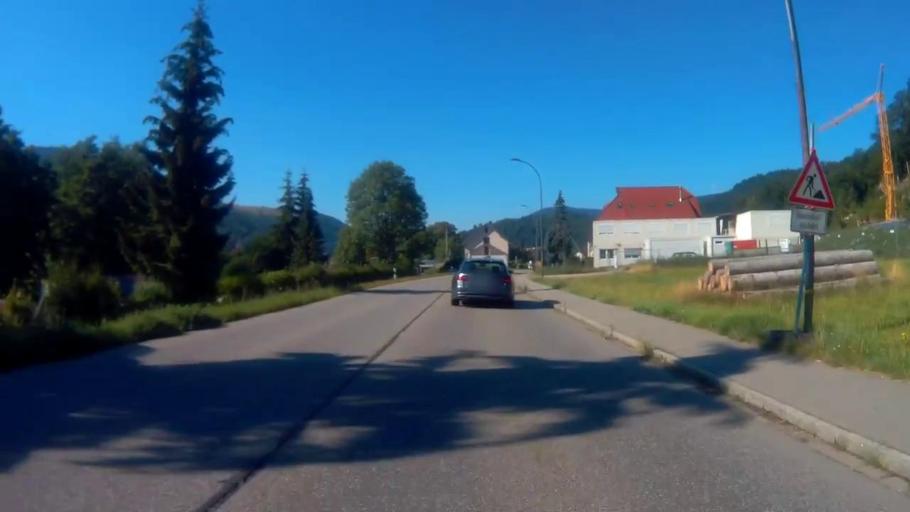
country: DE
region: Baden-Wuerttemberg
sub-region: Freiburg Region
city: Aitern
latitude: 47.7927
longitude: 7.9015
